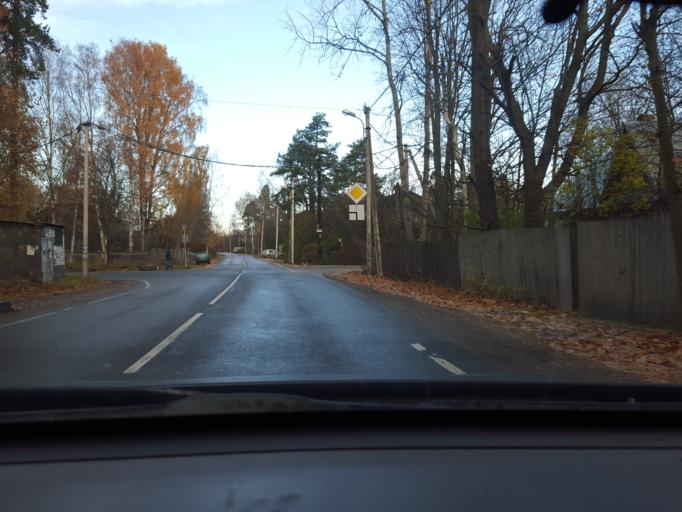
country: RU
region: St.-Petersburg
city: Shuvalovo
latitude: 60.0503
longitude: 30.2938
